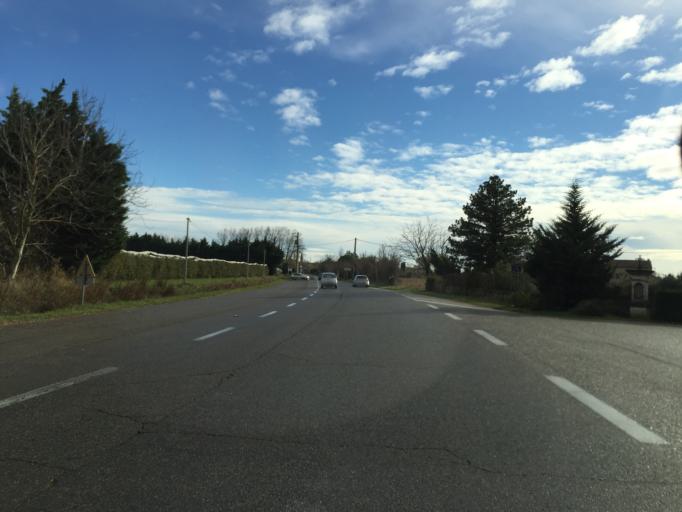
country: FR
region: Provence-Alpes-Cote d'Azur
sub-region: Departement du Vaucluse
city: Althen-des-Paluds
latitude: 43.9859
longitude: 4.9625
